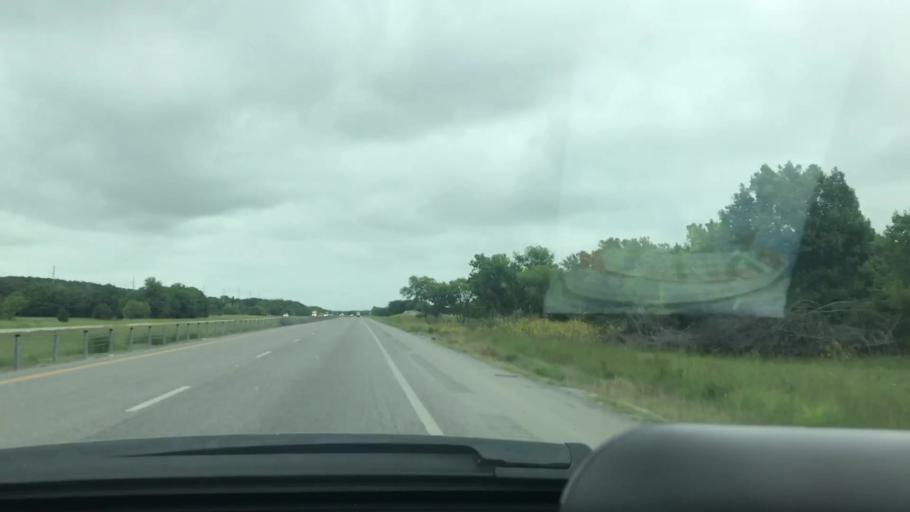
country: US
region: Oklahoma
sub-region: Coal County
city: Coalgate
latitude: 34.6330
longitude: -95.9551
